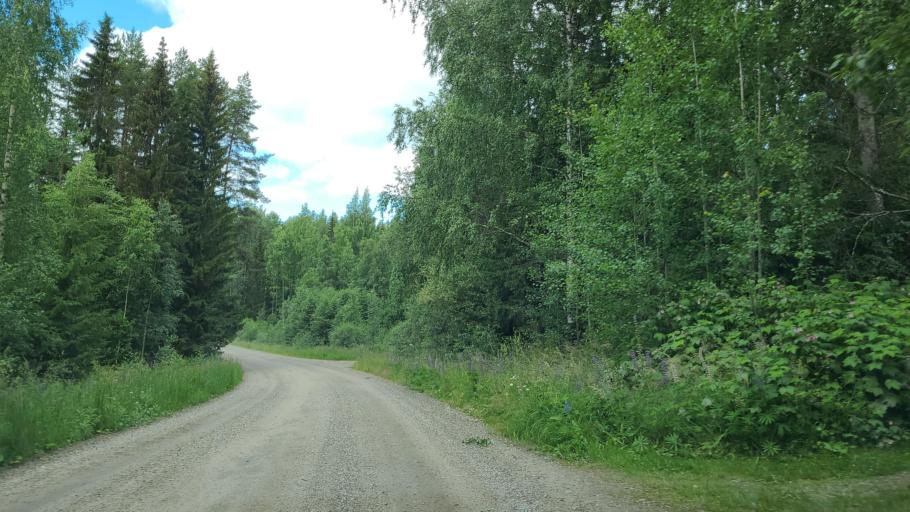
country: FI
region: Northern Savo
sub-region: Koillis-Savo
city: Kaavi
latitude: 62.9880
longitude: 28.5131
